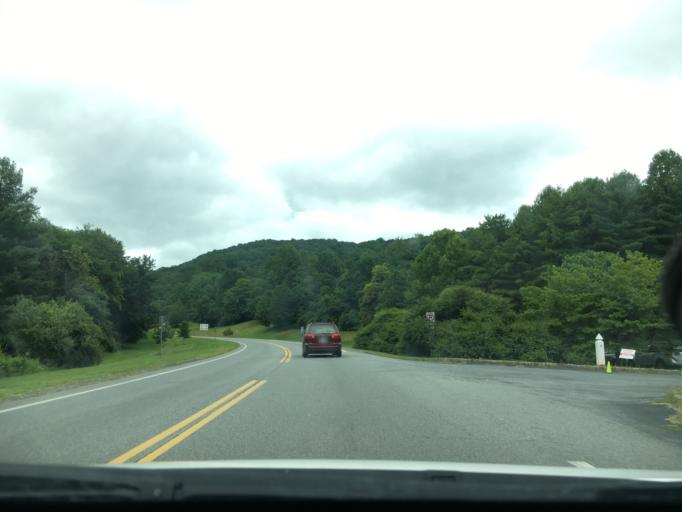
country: US
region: Virginia
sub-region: City of Charlottesville
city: Charlottesville
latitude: 38.0030
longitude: -78.4779
